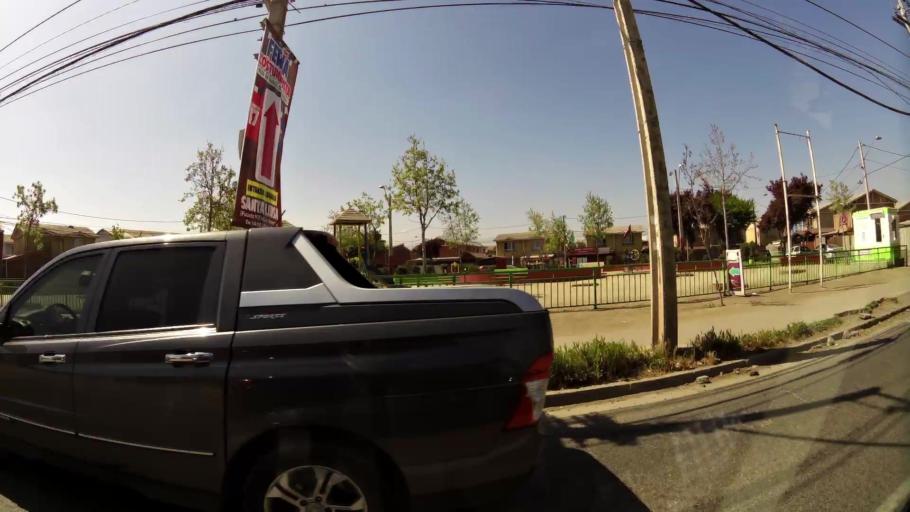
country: CL
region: Santiago Metropolitan
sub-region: Provincia de Santiago
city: Lo Prado
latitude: -33.3557
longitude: -70.7379
